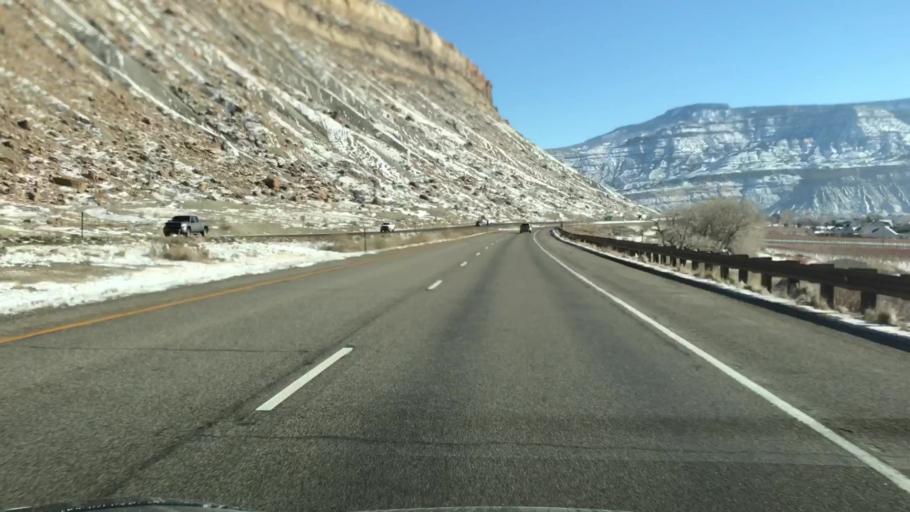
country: US
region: Colorado
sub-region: Mesa County
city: Palisade
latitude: 39.1203
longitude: -108.3714
